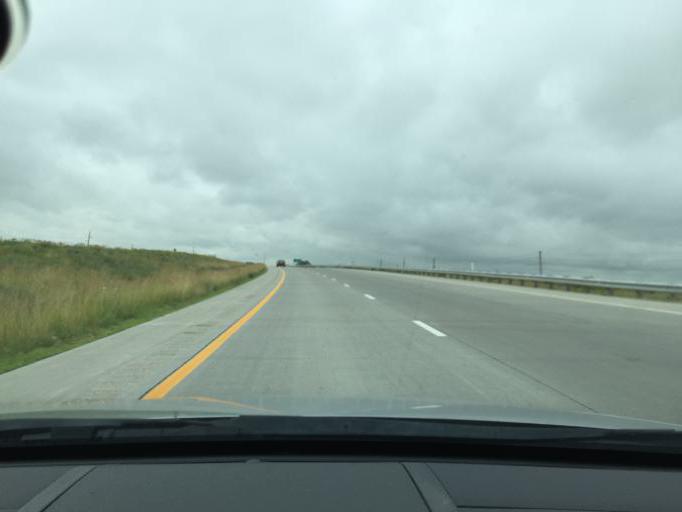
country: US
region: Kansas
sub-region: Reno County
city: South Hutchinson
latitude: 38.0132
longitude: -97.9275
